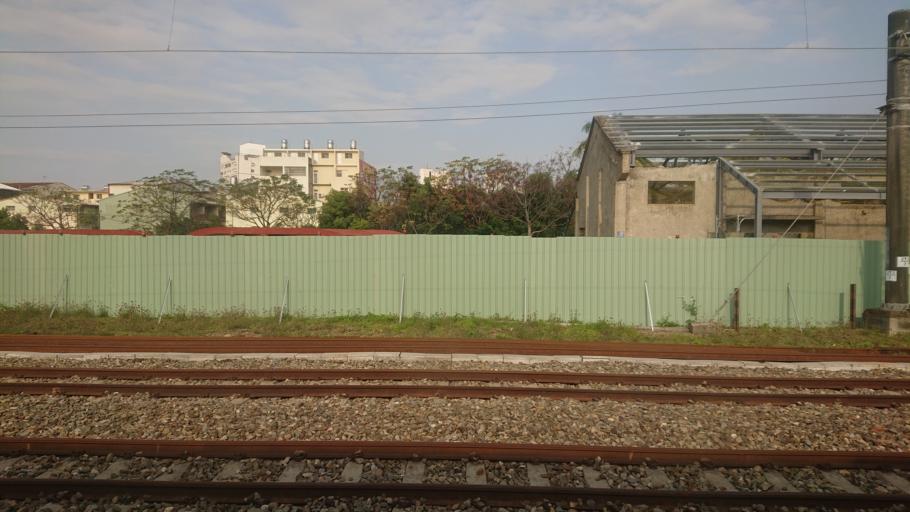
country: TW
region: Taiwan
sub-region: Yunlin
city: Douliu
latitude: 23.6718
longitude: 120.4801
